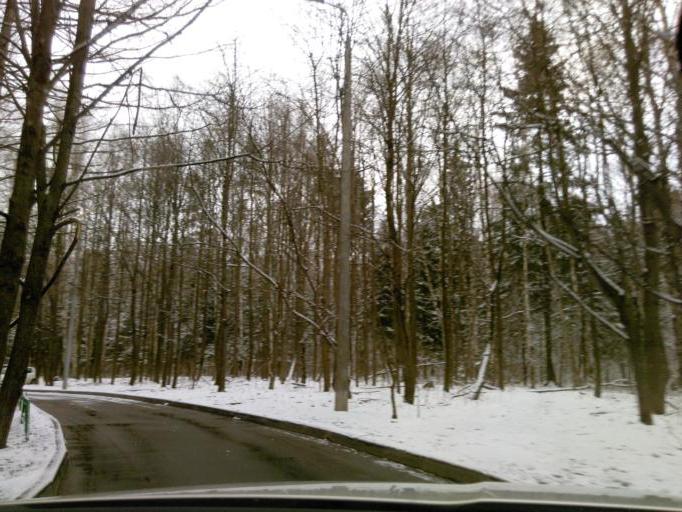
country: RU
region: Moskovskaya
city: Mendeleyevo
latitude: 56.0093
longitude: 37.2115
